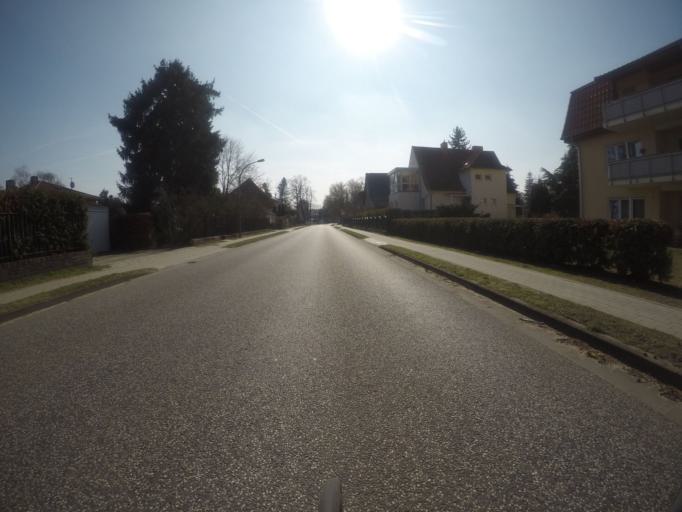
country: DE
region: Brandenburg
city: Konigs Wusterhausen
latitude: 52.3016
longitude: 13.6508
